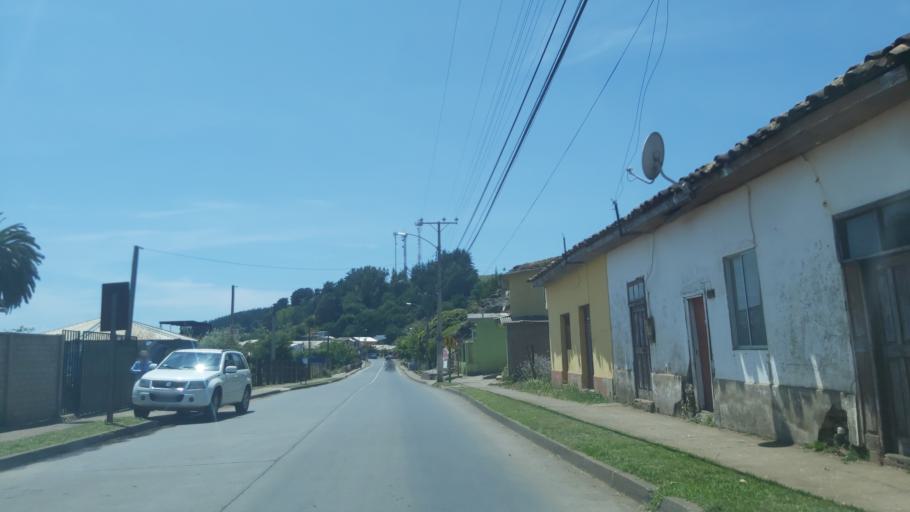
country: CL
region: Maule
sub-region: Provincia de Cauquenes
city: Cauquenes
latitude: -35.8440
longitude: -72.6325
